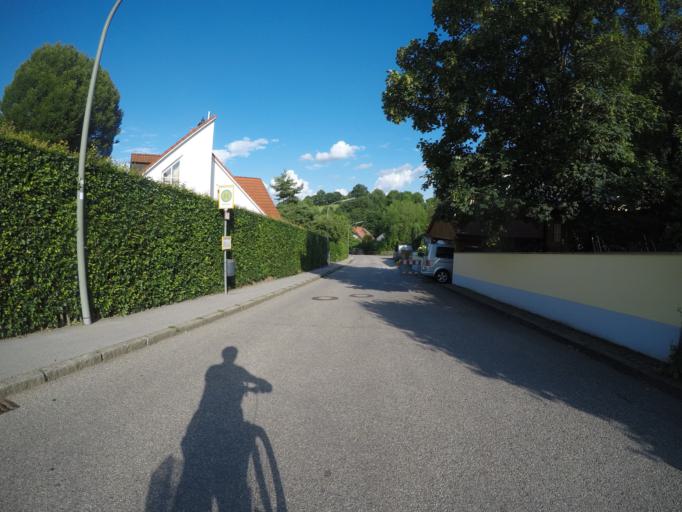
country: DE
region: Bavaria
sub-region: Lower Bavaria
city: Landshut
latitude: 48.5149
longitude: 12.1441
